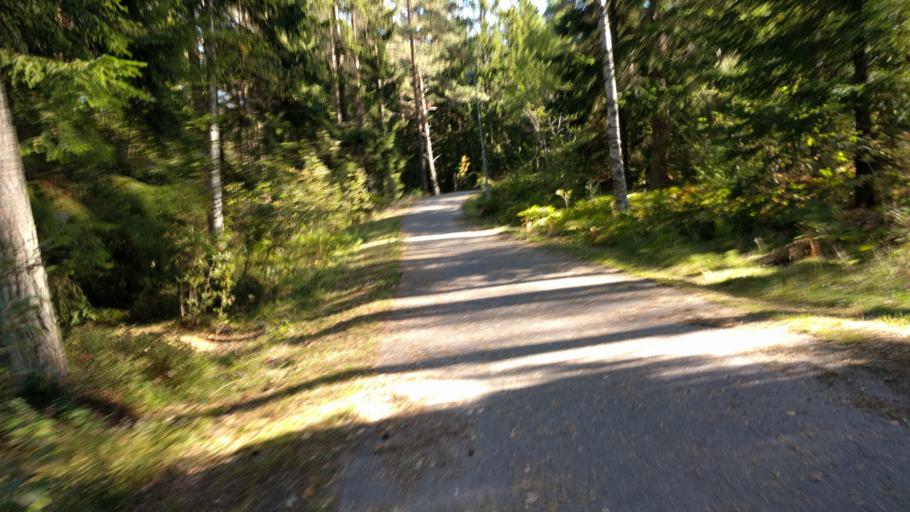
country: SE
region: Stockholm
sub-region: Vallentuna Kommun
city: Vallentuna
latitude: 59.4992
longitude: 18.0967
